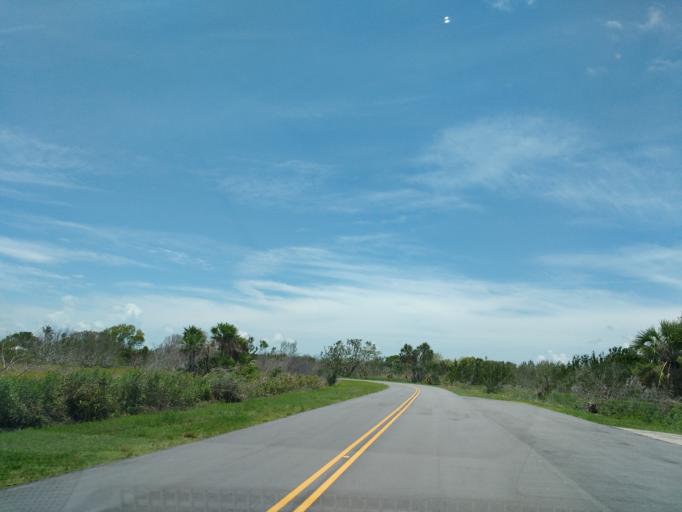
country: US
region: Florida
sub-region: Monroe County
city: Islamorada
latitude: 25.1387
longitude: -80.9373
